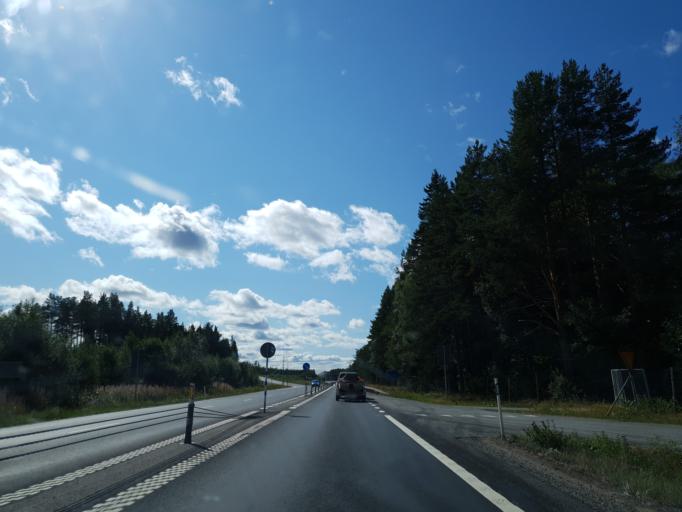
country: SE
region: Vaesterbotten
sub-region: Nordmalings Kommun
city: Nordmaling
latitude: 63.5526
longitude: 19.4182
